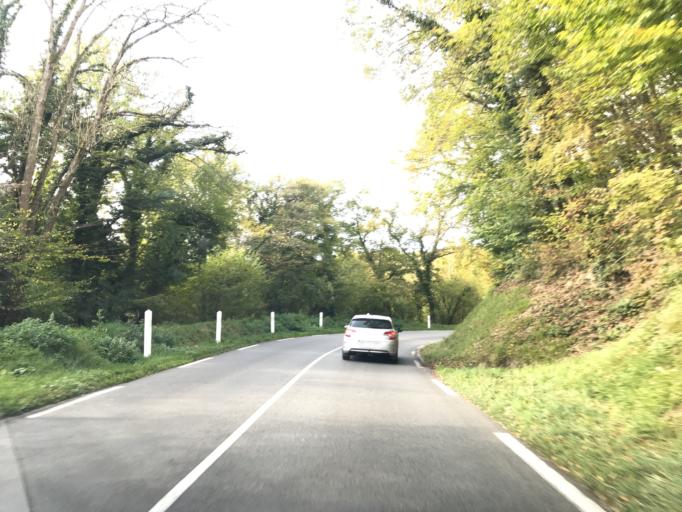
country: FR
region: Haute-Normandie
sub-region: Departement de l'Eure
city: Les Andelys
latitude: 49.2682
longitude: 1.4170
